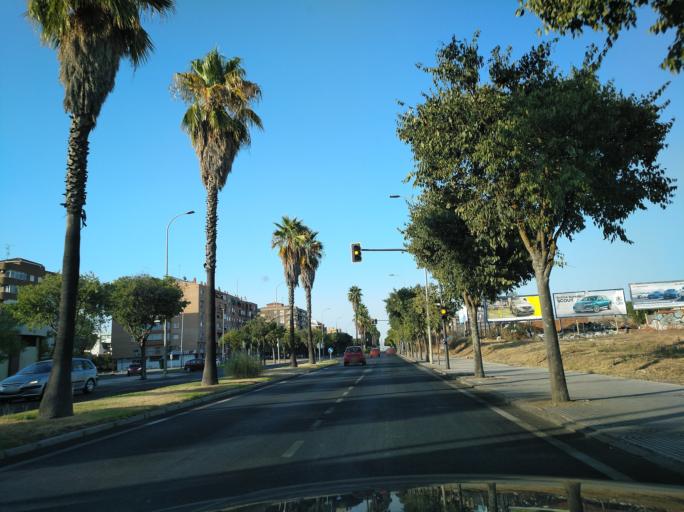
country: ES
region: Extremadura
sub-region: Provincia de Badajoz
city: Badajoz
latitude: 38.8620
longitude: -6.9854
